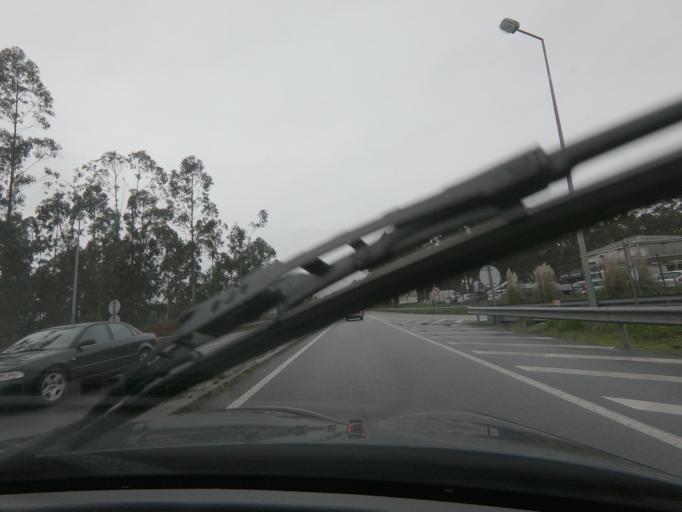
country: PT
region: Porto
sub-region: Vila do Conde
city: Arvore
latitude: 41.3029
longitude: -8.7010
